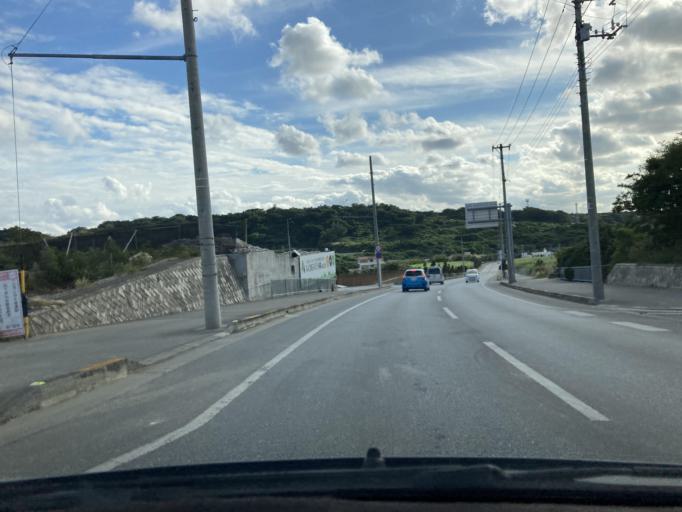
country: JP
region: Okinawa
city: Itoman
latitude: 26.1294
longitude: 127.6837
